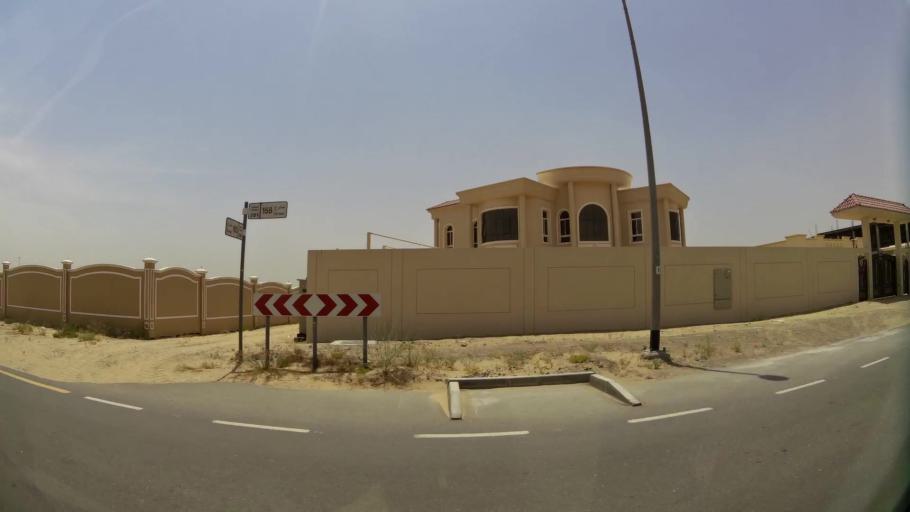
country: AE
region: Ash Shariqah
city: Sharjah
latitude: 25.2418
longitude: 55.4981
